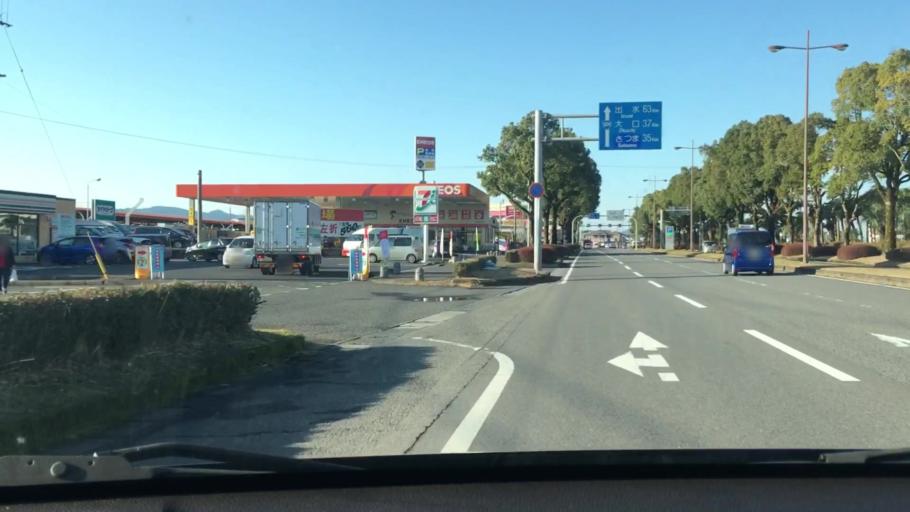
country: JP
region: Kagoshima
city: Kajiki
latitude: 31.7998
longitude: 130.7152
